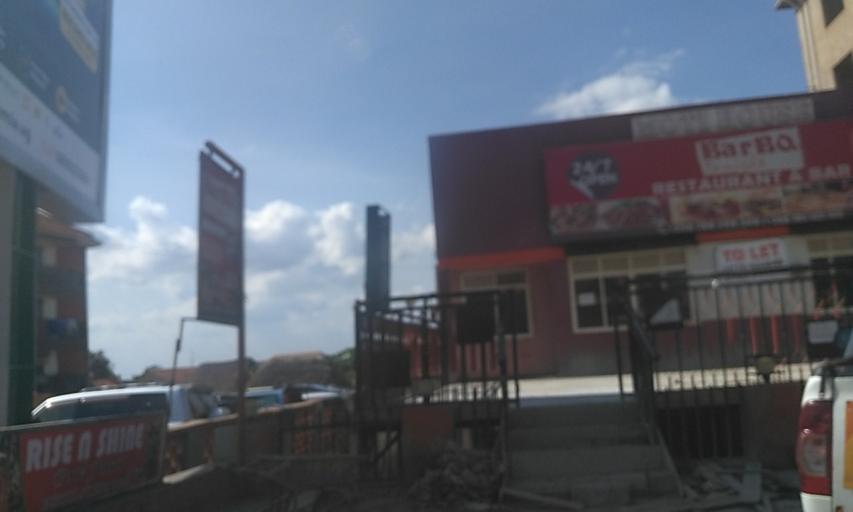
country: UG
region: Central Region
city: Kampala Central Division
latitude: 0.3510
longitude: 32.6058
